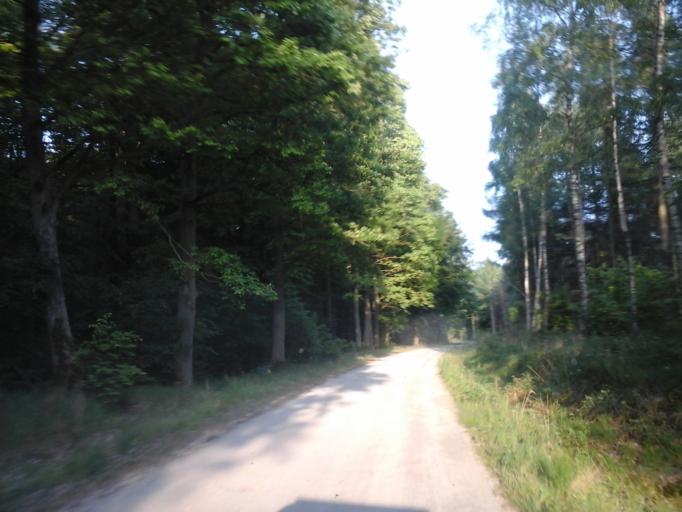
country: PL
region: West Pomeranian Voivodeship
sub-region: Powiat choszczenski
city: Krzecin
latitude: 52.9945
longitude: 15.4552
